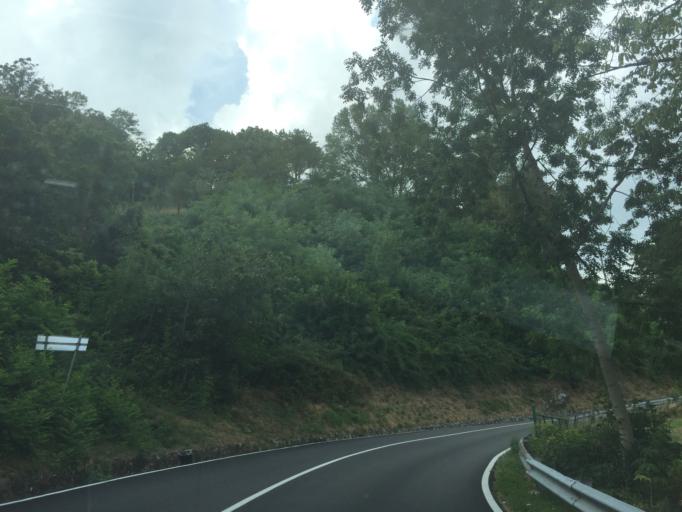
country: IT
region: Tuscany
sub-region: Provincia di Pistoia
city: Cutigliano
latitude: 44.1038
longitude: 10.7429
